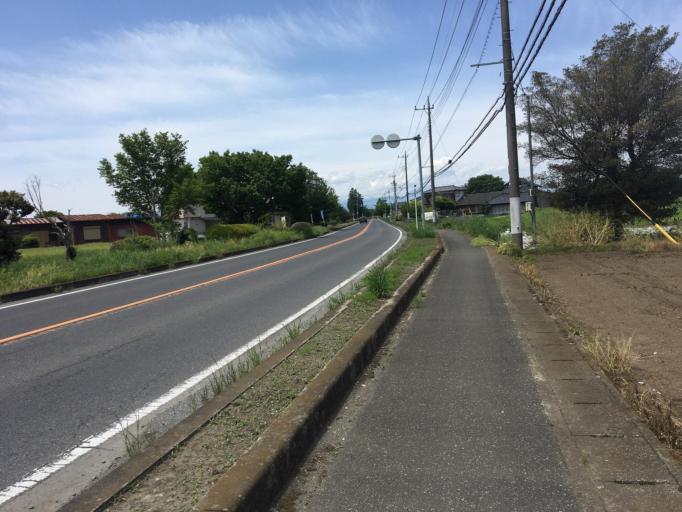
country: JP
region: Tochigi
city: Mibu
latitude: 36.4356
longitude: 139.7919
